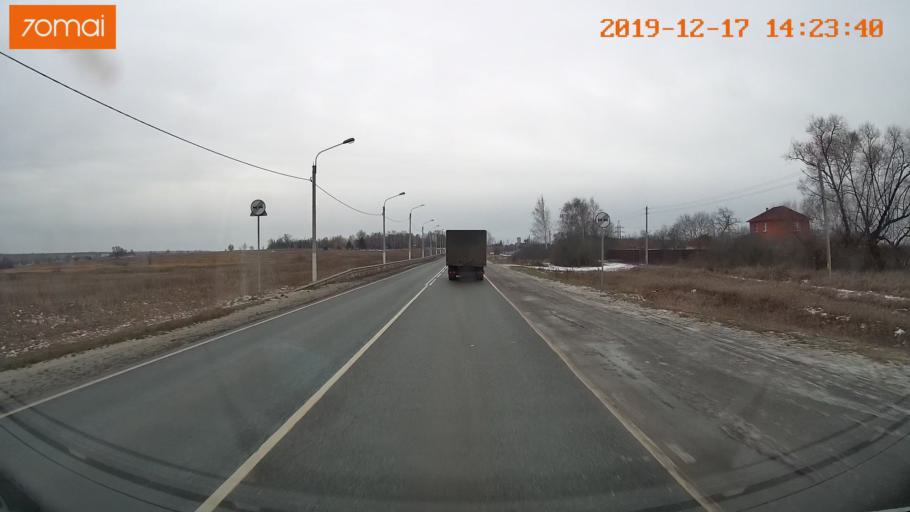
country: RU
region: Rjazan
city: Zakharovo
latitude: 54.4086
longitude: 39.3557
